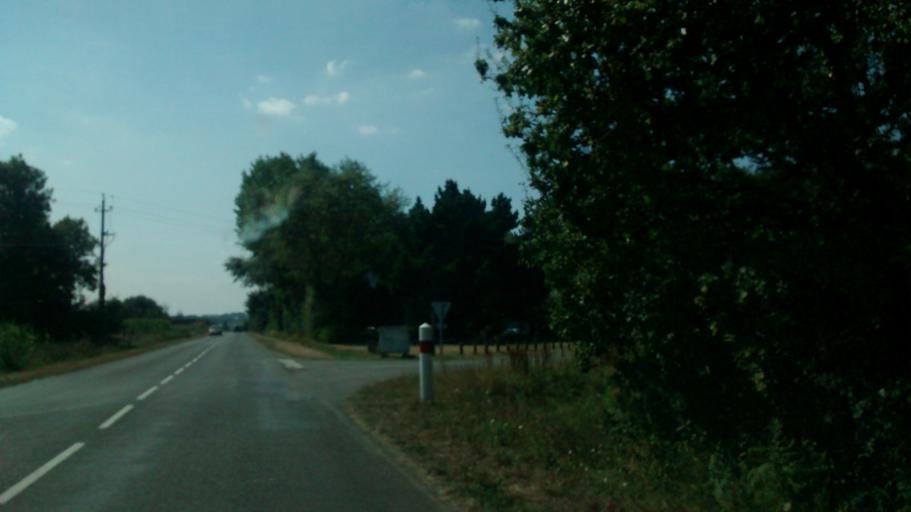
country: FR
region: Brittany
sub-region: Departement d'Ille-et-Vilaine
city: Cancale
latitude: 48.6935
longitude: -1.8656
